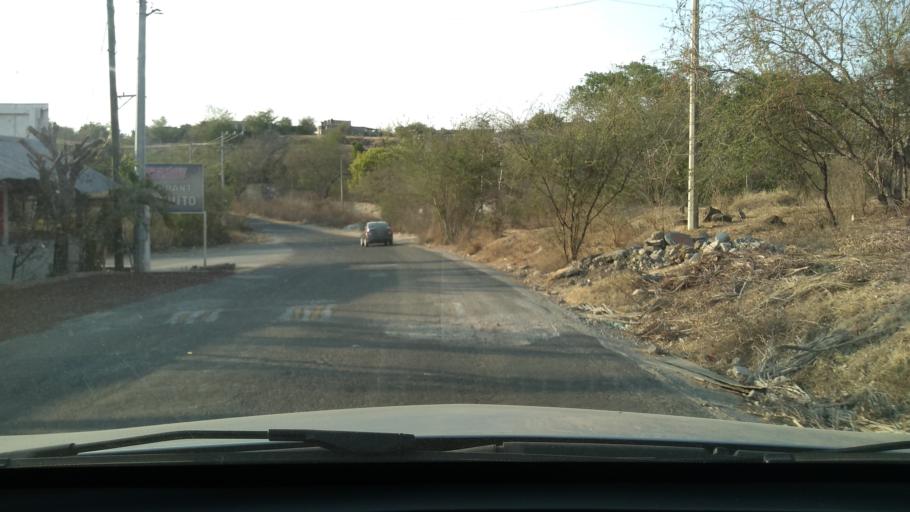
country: MX
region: Morelos
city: Puente de Ixtla
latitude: 18.6039
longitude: -99.3125
